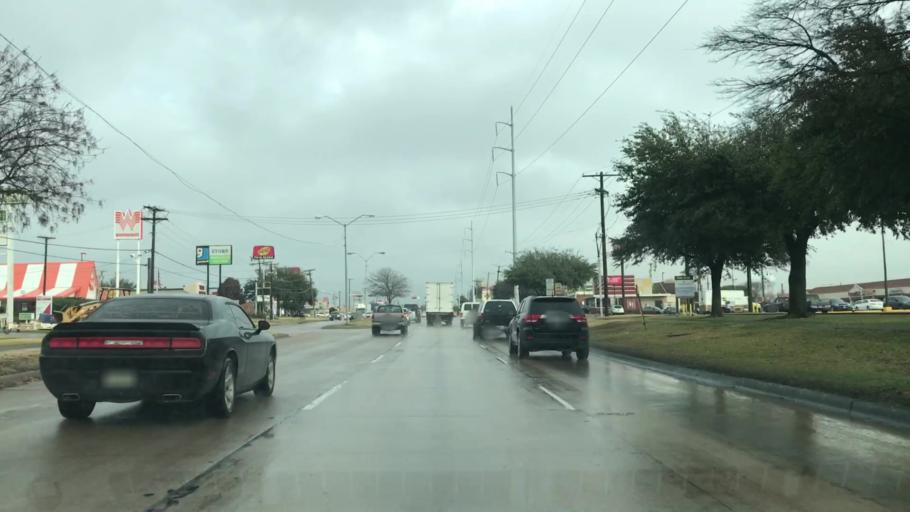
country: US
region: Texas
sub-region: Dallas County
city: Irving
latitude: 32.8453
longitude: -96.9923
